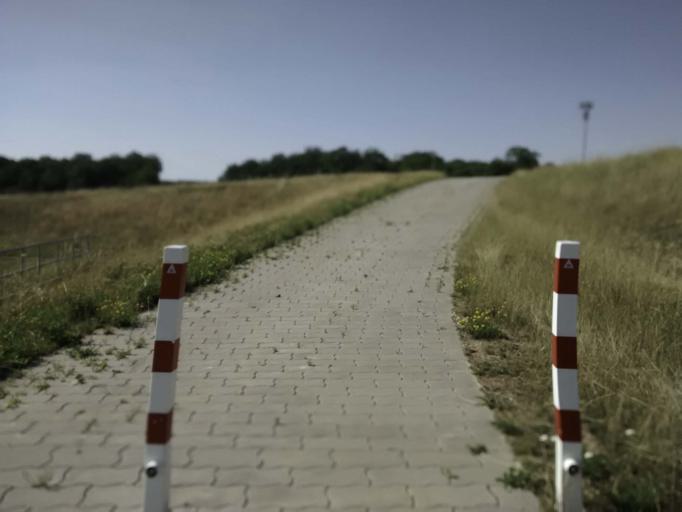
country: DE
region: Saxony-Anhalt
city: Wulfen
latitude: 51.8845
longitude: 11.9697
